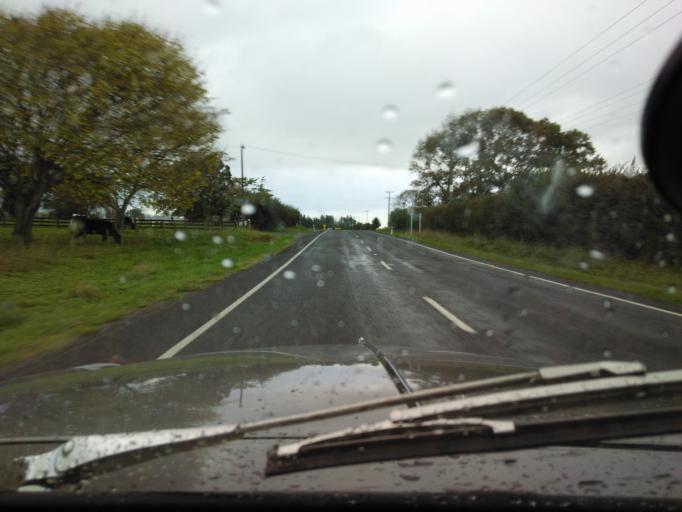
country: NZ
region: Waikato
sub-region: Hauraki District
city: Paeroa
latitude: -37.5644
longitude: 175.5075
